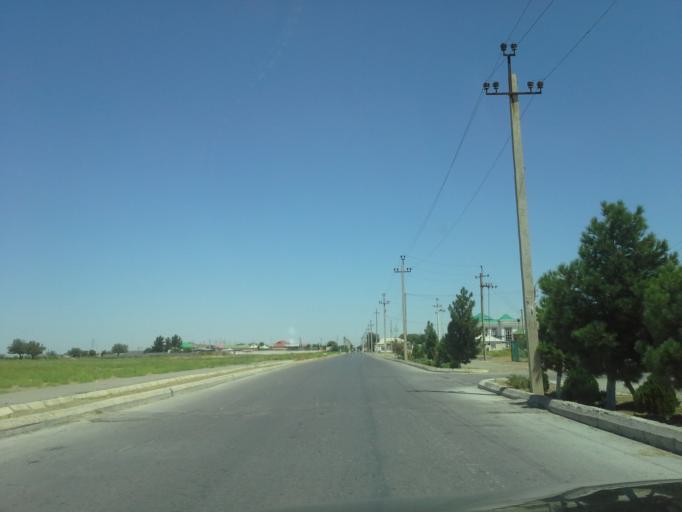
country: TM
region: Ahal
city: Abadan
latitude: 38.0342
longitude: 58.2647
